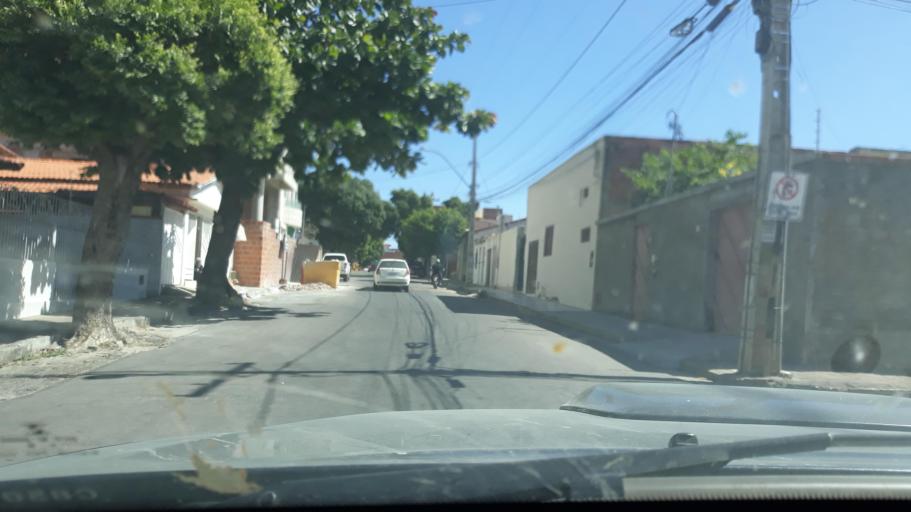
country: BR
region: Bahia
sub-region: Guanambi
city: Guanambi
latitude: -14.2210
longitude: -42.7831
